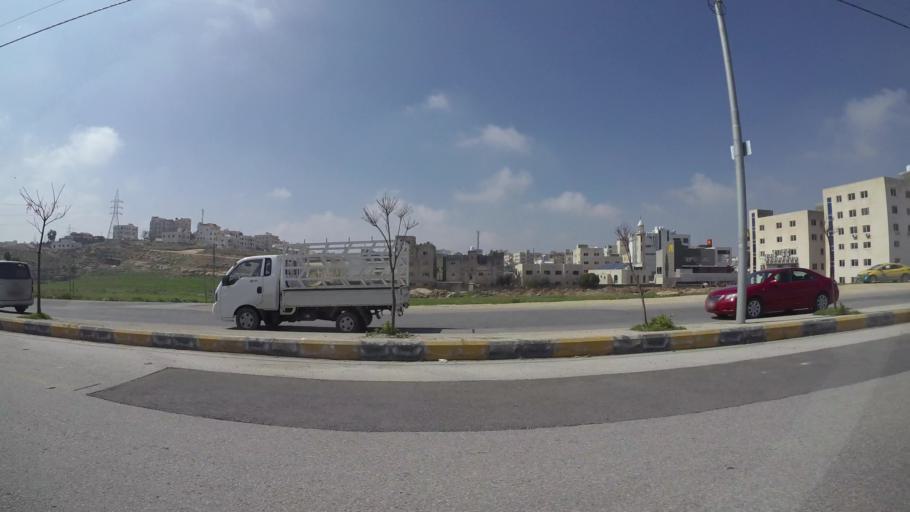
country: JO
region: Amman
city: Al Bunayyat ash Shamaliyah
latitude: 31.8951
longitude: 35.9039
